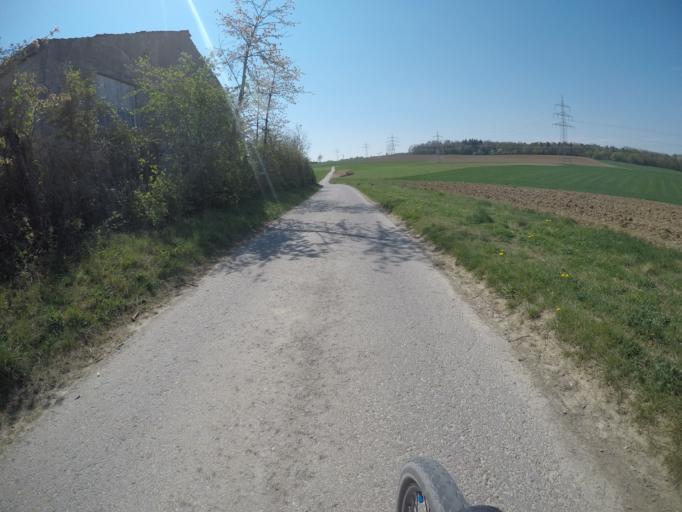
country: DE
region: Baden-Wuerttemberg
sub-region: Regierungsbezirk Stuttgart
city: Leonberg
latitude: 48.8356
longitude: 9.0015
